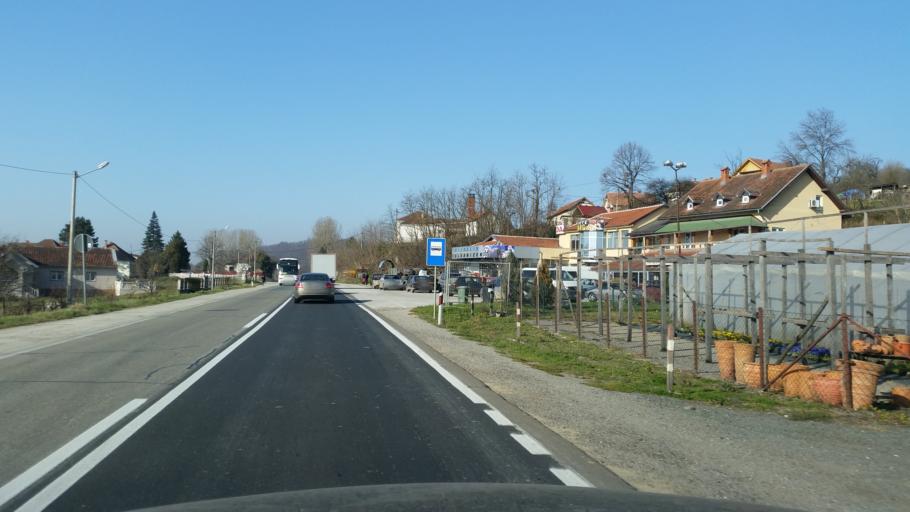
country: RS
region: Central Serbia
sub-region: Kolubarski Okrug
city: Lajkovac
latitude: 44.3358
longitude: 20.2137
